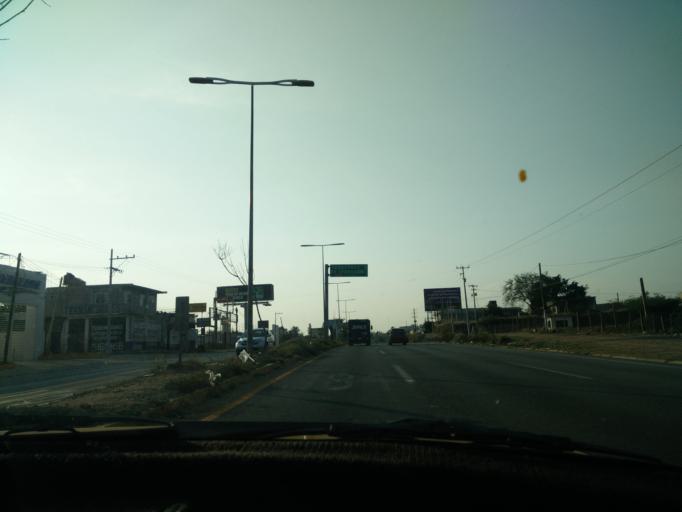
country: MX
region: Oaxaca
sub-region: Santa Maria Atzompa
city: Fraccionamiento Riberas de San Jeronimo
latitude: 17.1317
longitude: -96.7717
